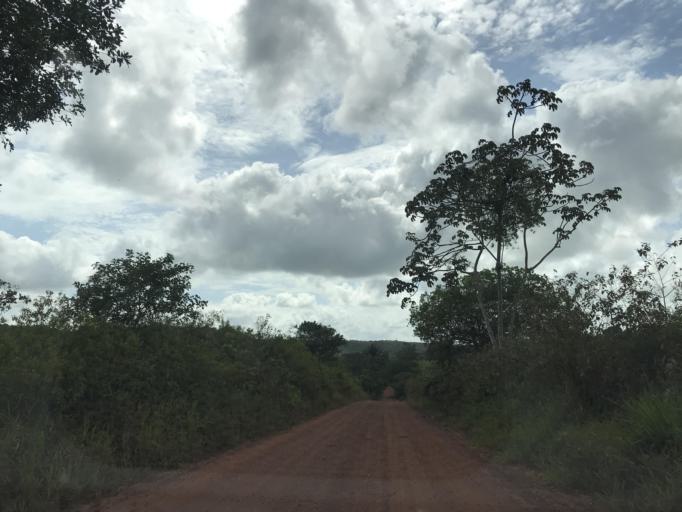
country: BR
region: Bahia
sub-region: Entre Rios
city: Entre Rios
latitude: -12.1740
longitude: -38.1323
